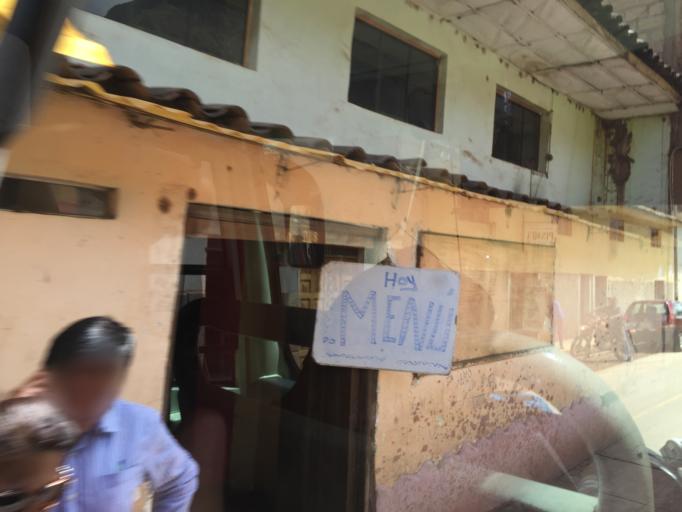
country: PE
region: Cusco
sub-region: Provincia de Calca
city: Pisac
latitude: -13.4230
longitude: -71.8516
